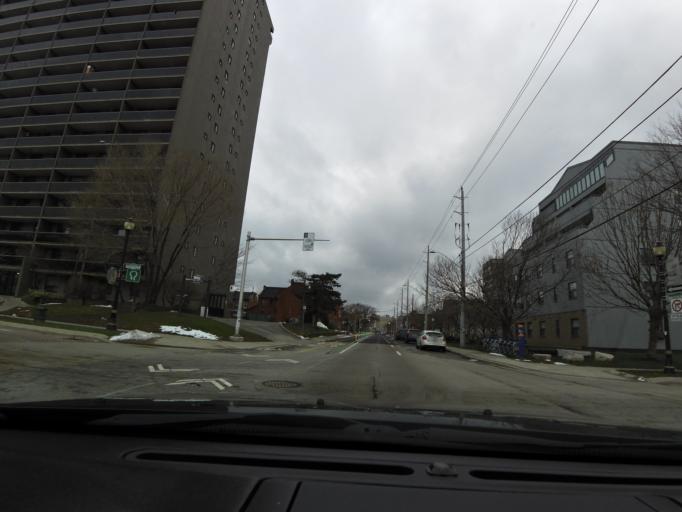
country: CA
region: Ontario
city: Hamilton
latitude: 43.2517
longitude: -79.8629
